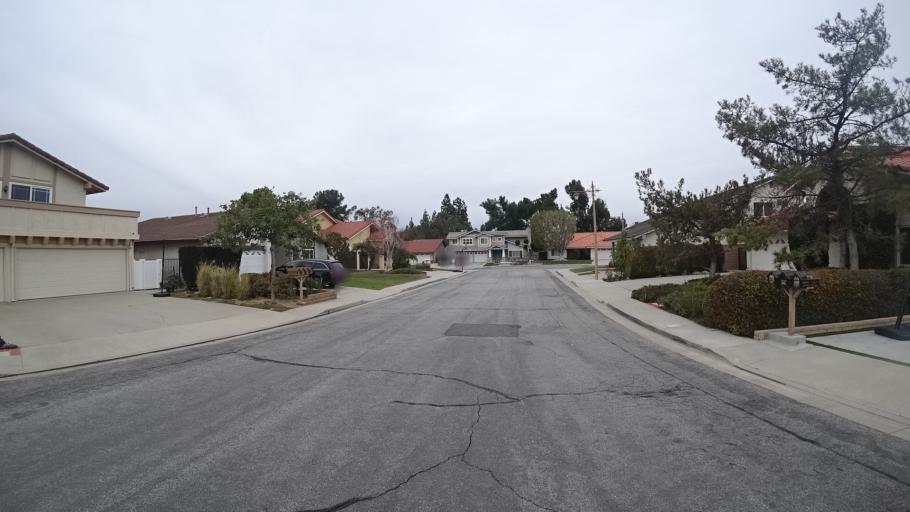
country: US
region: California
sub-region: Orange County
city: Villa Park
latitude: 33.8402
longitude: -117.7447
